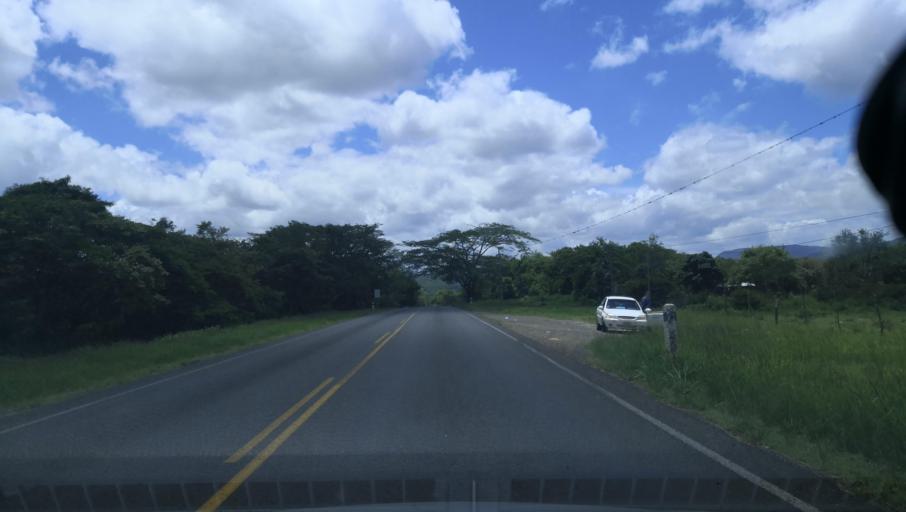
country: NI
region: Esteli
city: Esteli
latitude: 13.2253
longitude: -86.3789
